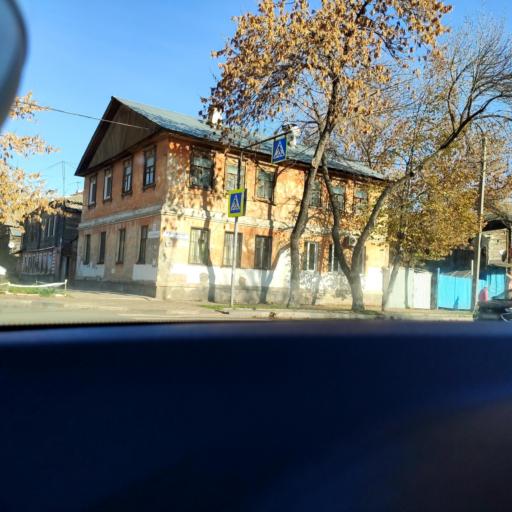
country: RU
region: Samara
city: Samara
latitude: 53.1938
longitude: 50.1184
